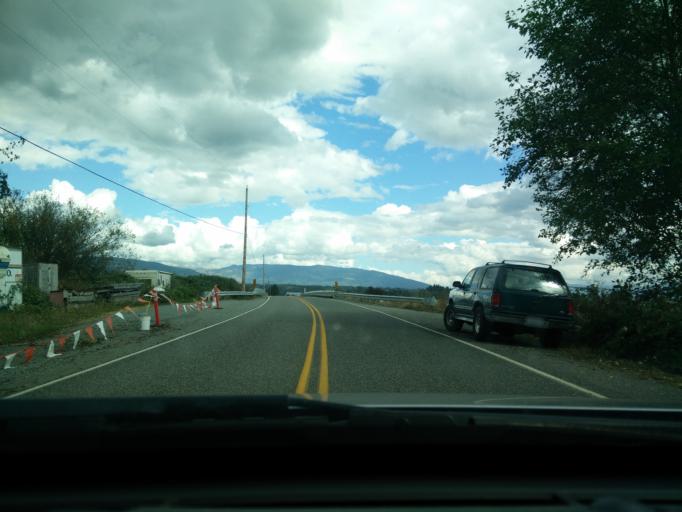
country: US
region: Washington
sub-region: Skagit County
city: Burlington
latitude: 48.5541
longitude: -122.4554
